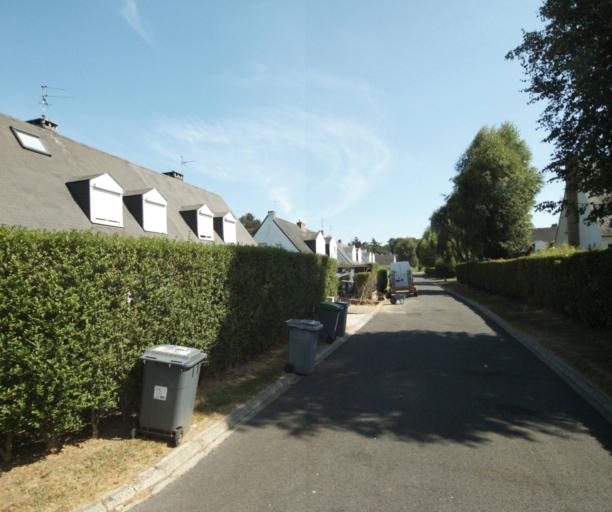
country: FR
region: Nord-Pas-de-Calais
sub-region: Departement du Nord
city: Bondues
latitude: 50.7082
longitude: 3.0814
